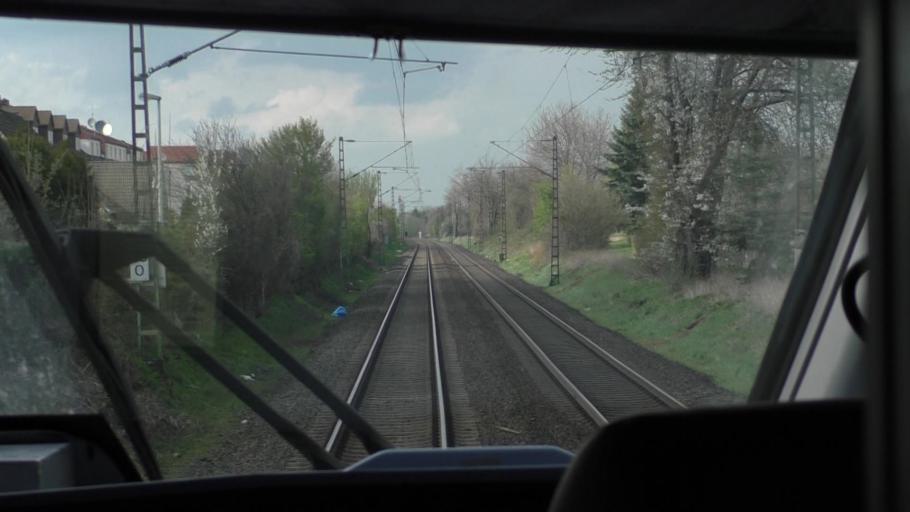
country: DE
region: North Rhine-Westphalia
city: Bornheim
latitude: 50.7582
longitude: 7.0096
